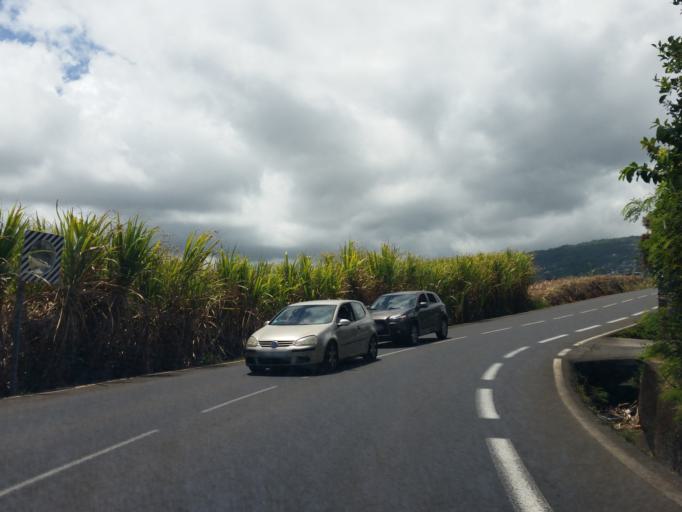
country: RE
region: Reunion
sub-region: Reunion
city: Sainte-Marie
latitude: -20.9125
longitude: 55.5198
